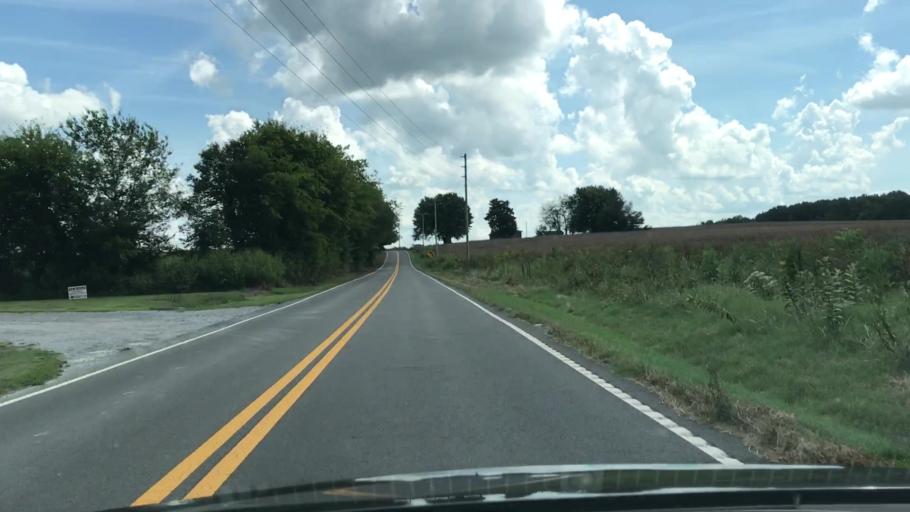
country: US
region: Tennessee
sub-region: Robertson County
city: Springfield
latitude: 36.5679
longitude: -86.8561
